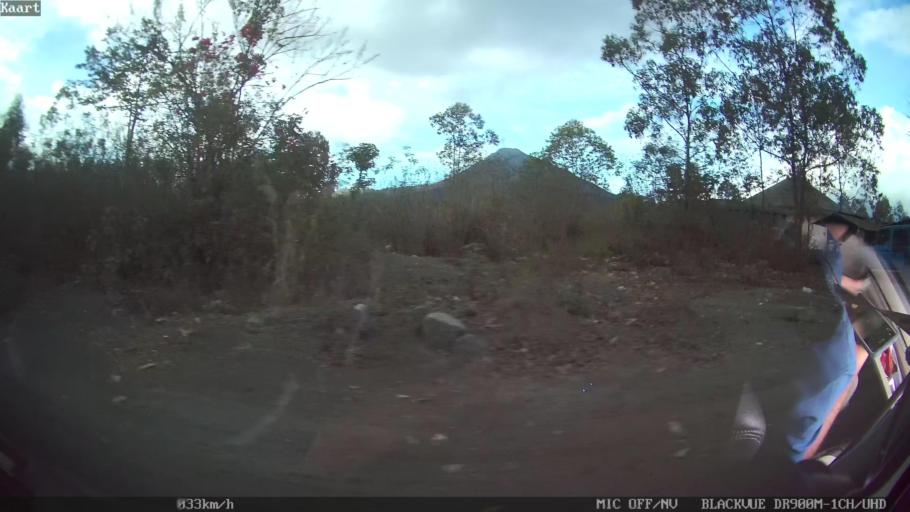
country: ID
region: Bali
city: Banjar Kedisan
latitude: -8.2570
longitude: 115.3503
